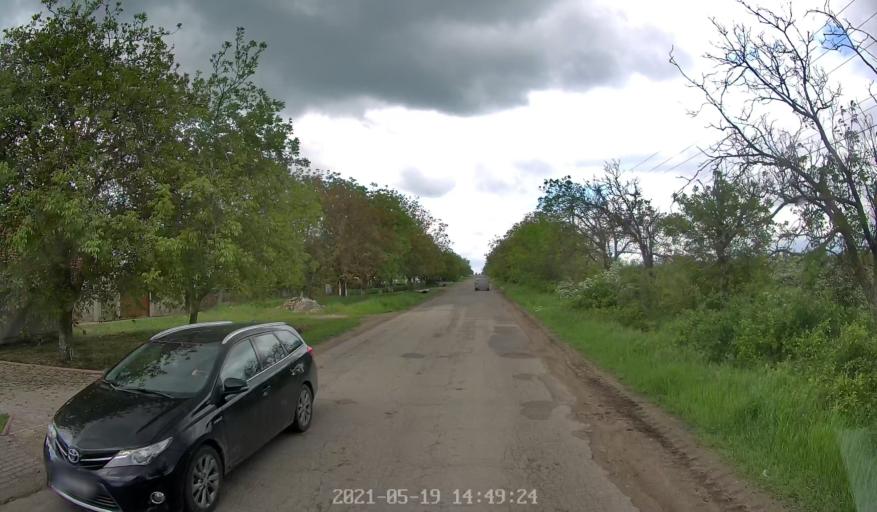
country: MD
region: Chisinau
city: Stauceni
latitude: 47.0497
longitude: 28.9518
